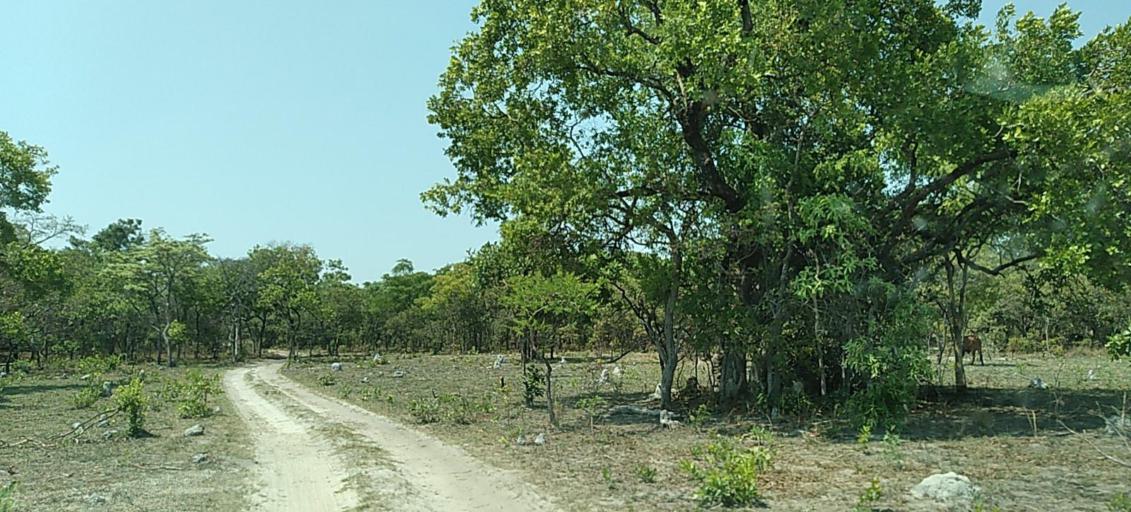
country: ZM
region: Copperbelt
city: Mpongwe
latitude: -13.8454
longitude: 28.0559
